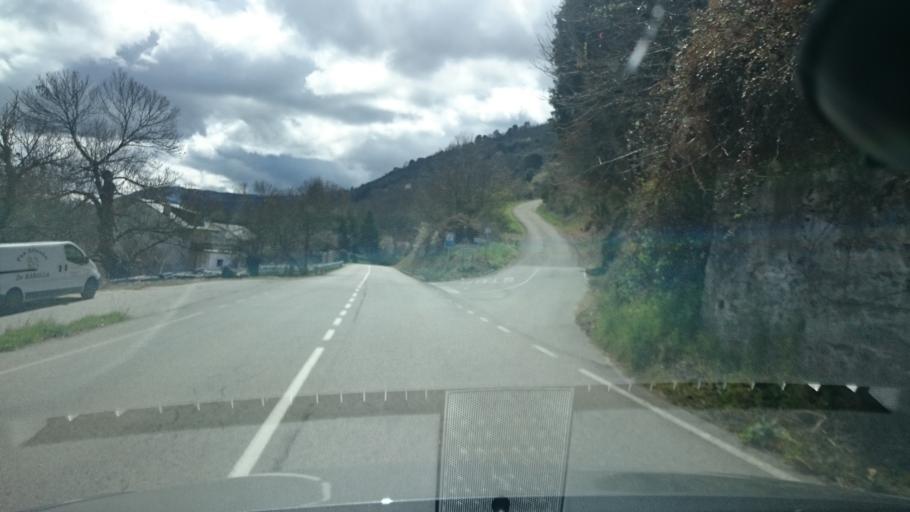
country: ES
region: Castille and Leon
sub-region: Provincia de Leon
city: Villafranca del Bierzo
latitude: 42.6051
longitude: -6.8188
